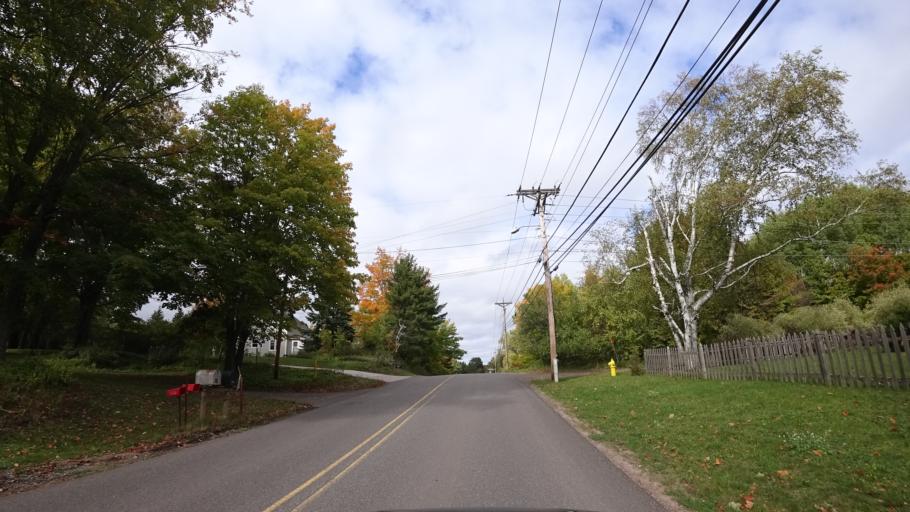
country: US
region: Michigan
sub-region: Marquette County
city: Trowbridge Park
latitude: 46.5458
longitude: -87.4374
